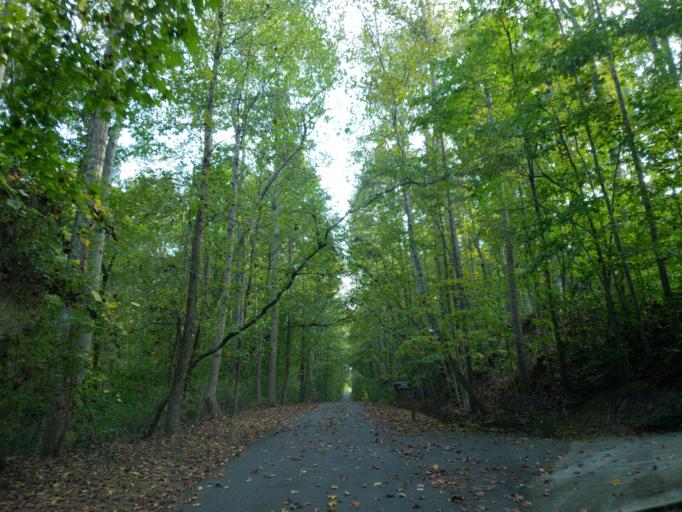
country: US
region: Georgia
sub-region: Fulton County
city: Roswell
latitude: 34.0828
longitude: -84.4069
